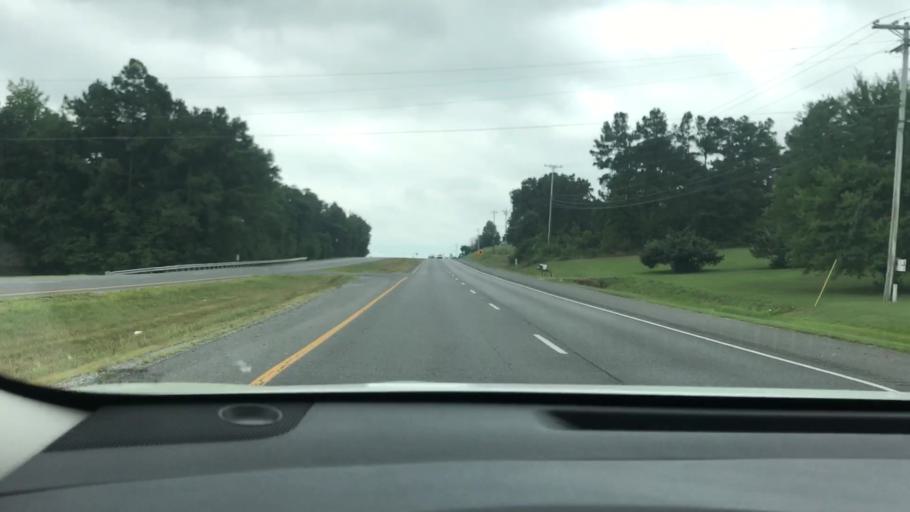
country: US
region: Kentucky
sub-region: Calloway County
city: Murray
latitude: 36.6725
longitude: -88.3030
